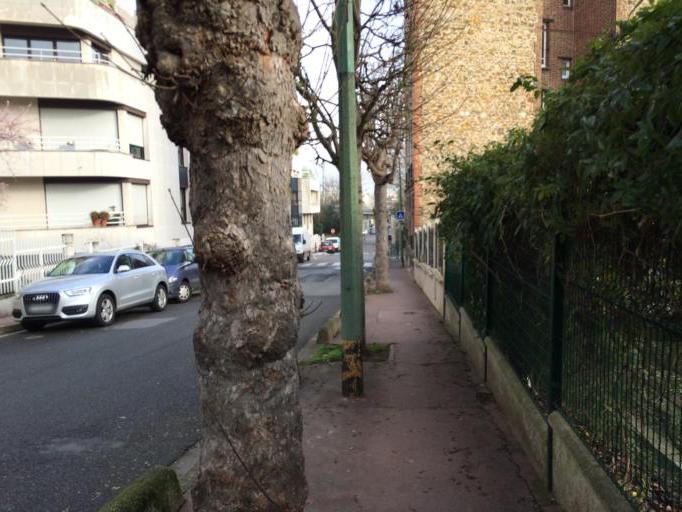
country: FR
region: Ile-de-France
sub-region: Departement des Hauts-de-Seine
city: Suresnes
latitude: 48.8640
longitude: 2.2197
